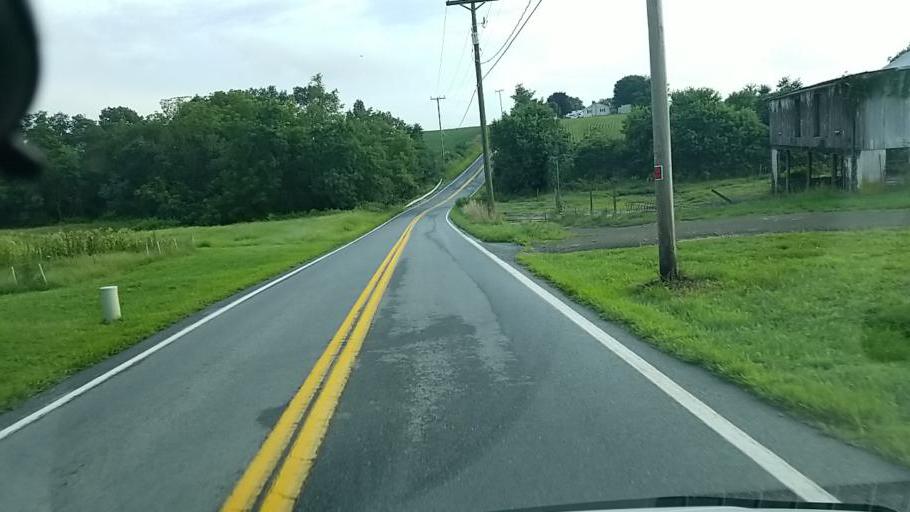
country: US
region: Pennsylvania
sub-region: Cumberland County
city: Newville
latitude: 40.2280
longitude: -77.4551
